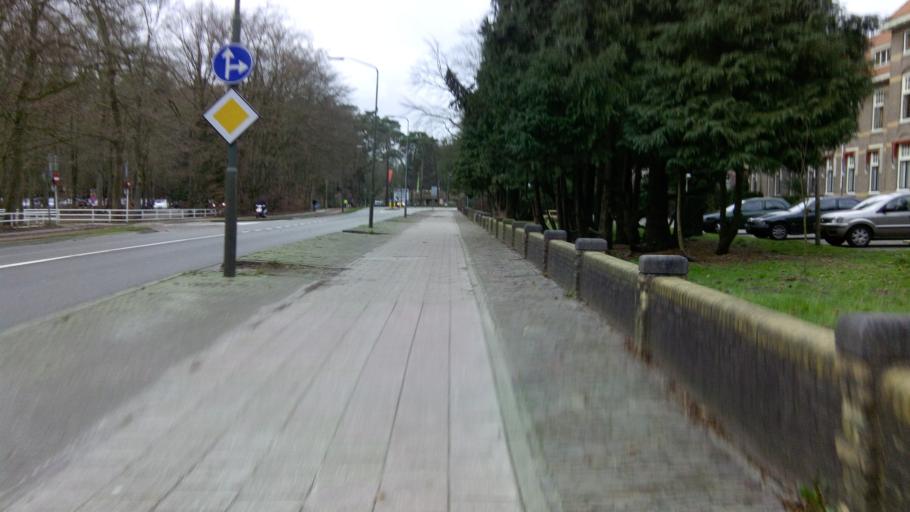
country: NL
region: Utrecht
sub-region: Gemeente Amersfoort
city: Amersfoort
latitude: 52.1513
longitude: 5.3522
